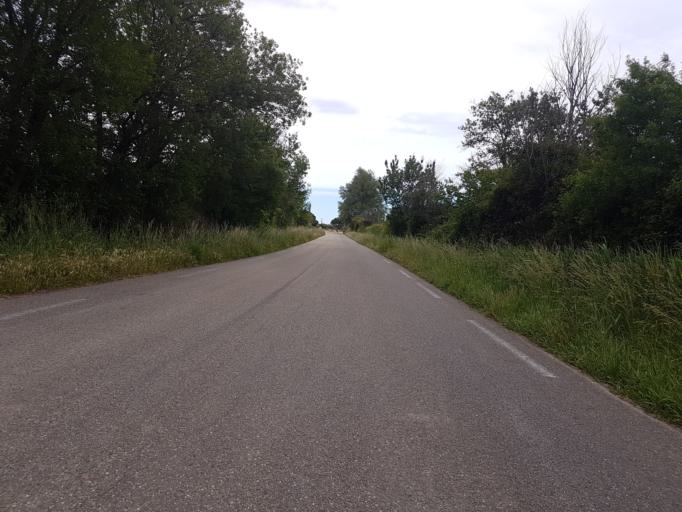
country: FR
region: Languedoc-Roussillon
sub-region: Departement du Gard
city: Saint-Gilles
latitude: 43.6685
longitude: 4.4409
